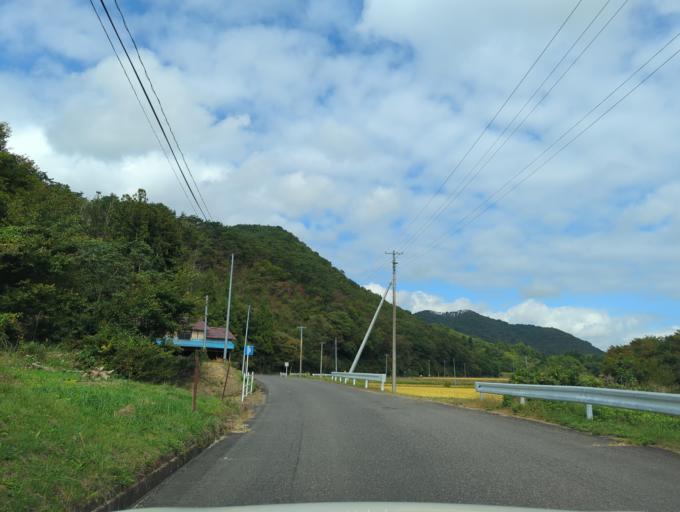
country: JP
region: Fukushima
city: Motomiya
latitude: 37.5022
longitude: 140.3259
